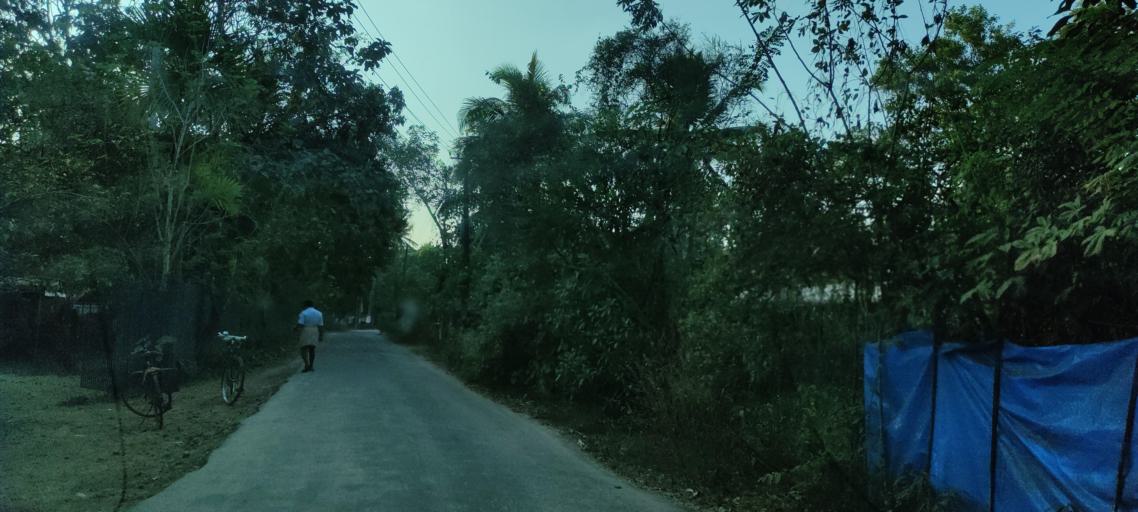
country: IN
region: Kerala
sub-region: Alappuzha
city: Vayalar
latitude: 9.7274
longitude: 76.3567
